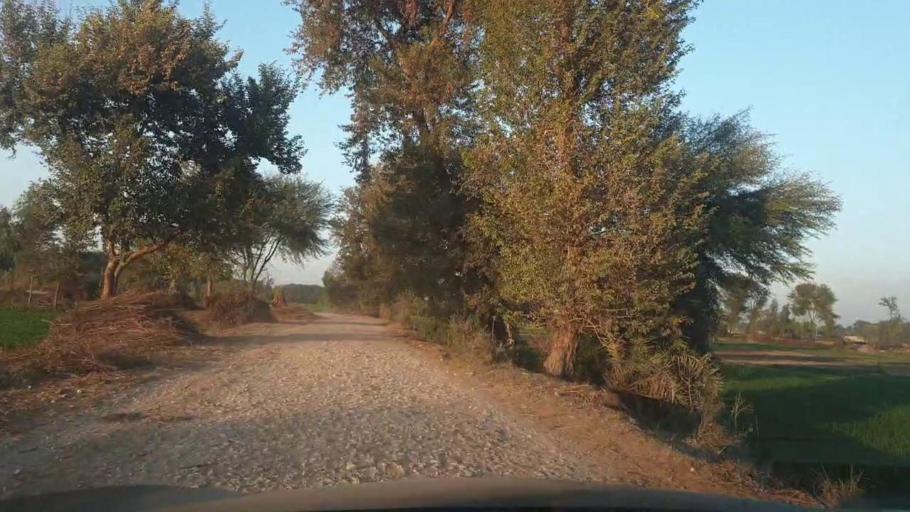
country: PK
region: Sindh
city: Ubauro
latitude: 28.1829
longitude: 69.6026
